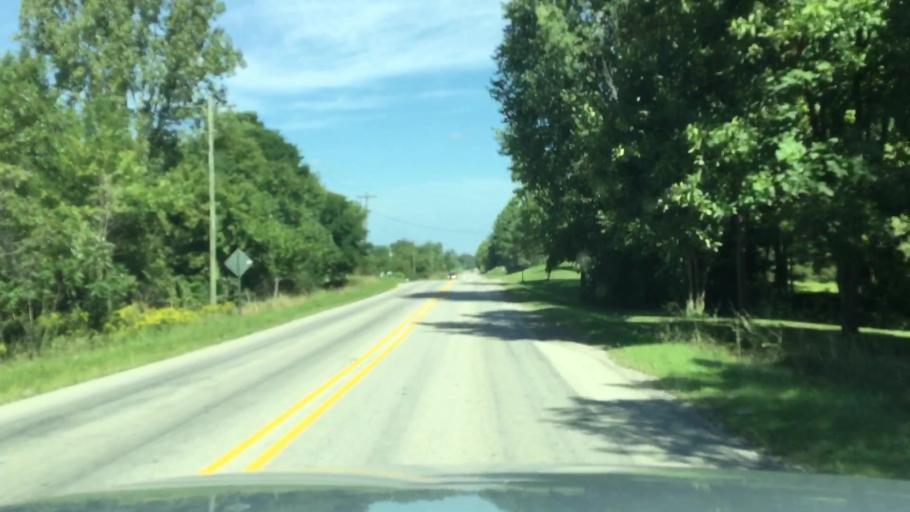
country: US
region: Michigan
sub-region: Lenawee County
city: Manitou Beach-Devils Lake
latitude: 42.0112
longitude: -84.2761
